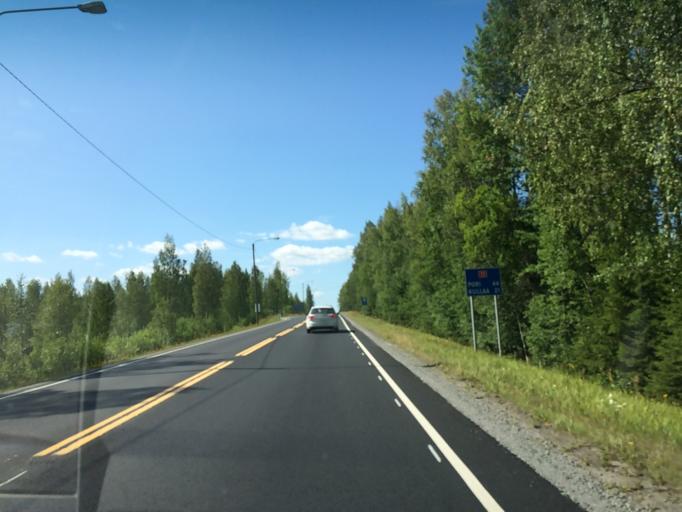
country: FI
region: Pirkanmaa
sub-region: Lounais-Pirkanmaa
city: Kiikoinen
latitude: 61.4750
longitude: 22.5553
